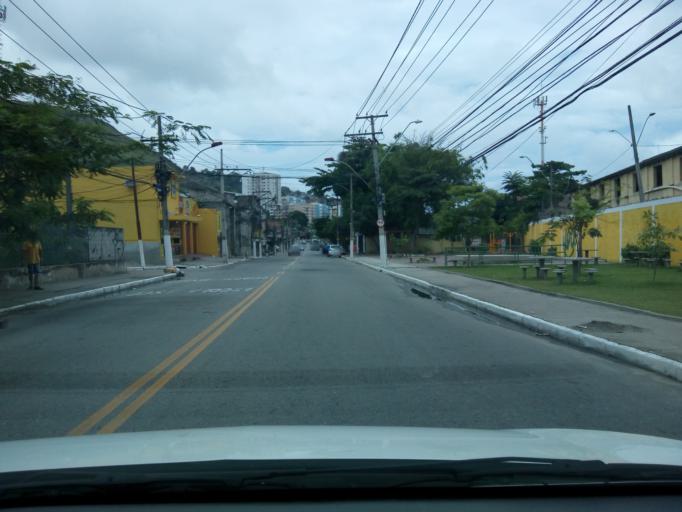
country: BR
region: Rio de Janeiro
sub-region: Niteroi
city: Niteroi
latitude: -22.8686
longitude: -43.1043
